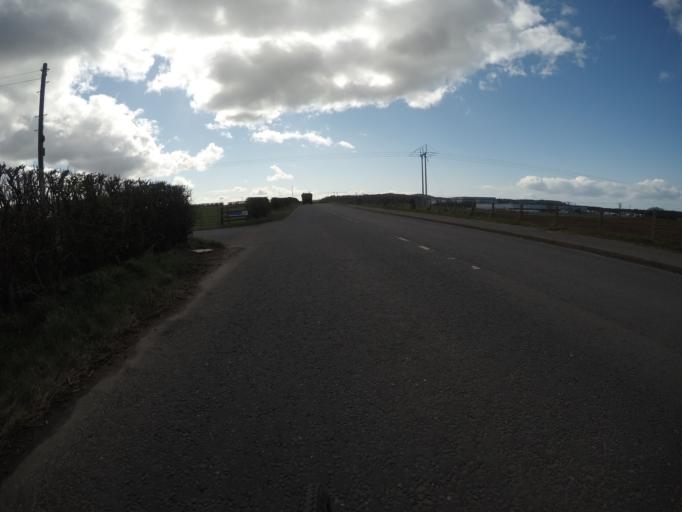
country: GB
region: Scotland
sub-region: North Ayrshire
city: Dreghorn
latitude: 55.5922
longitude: -4.6024
